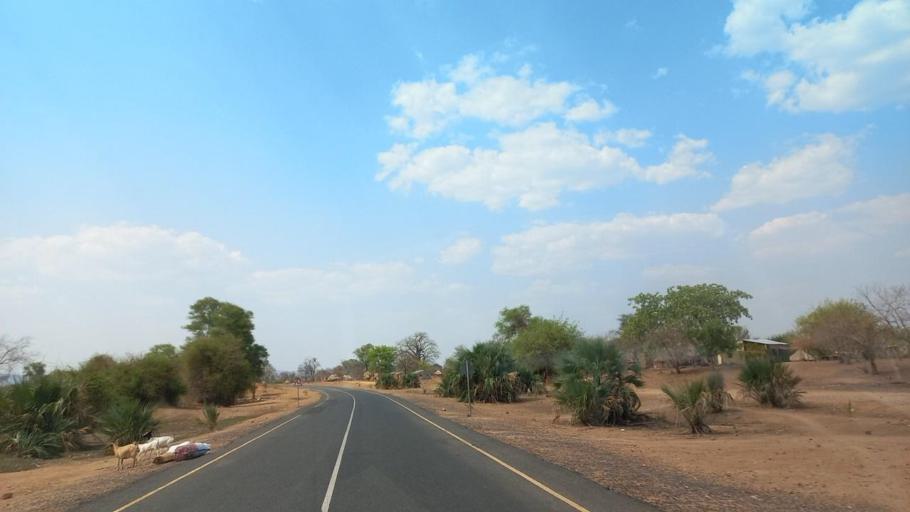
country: ZM
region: Lusaka
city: Luangwa
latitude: -15.1345
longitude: 30.2067
